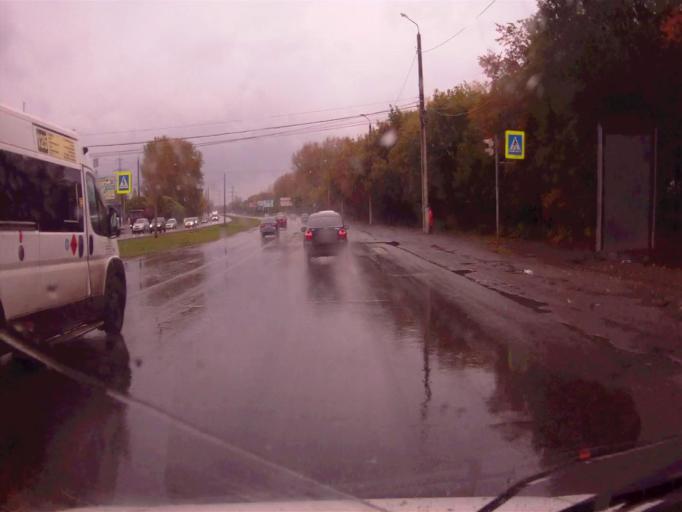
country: RU
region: Chelyabinsk
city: Dolgoderevenskoye
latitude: 55.2415
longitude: 61.3611
